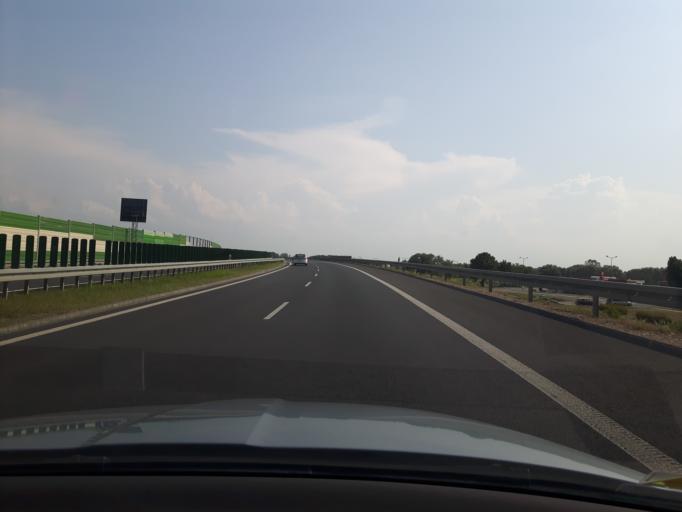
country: PL
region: Masovian Voivodeship
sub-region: Powiat plonski
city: Plonsk
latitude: 52.6157
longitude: 20.3877
